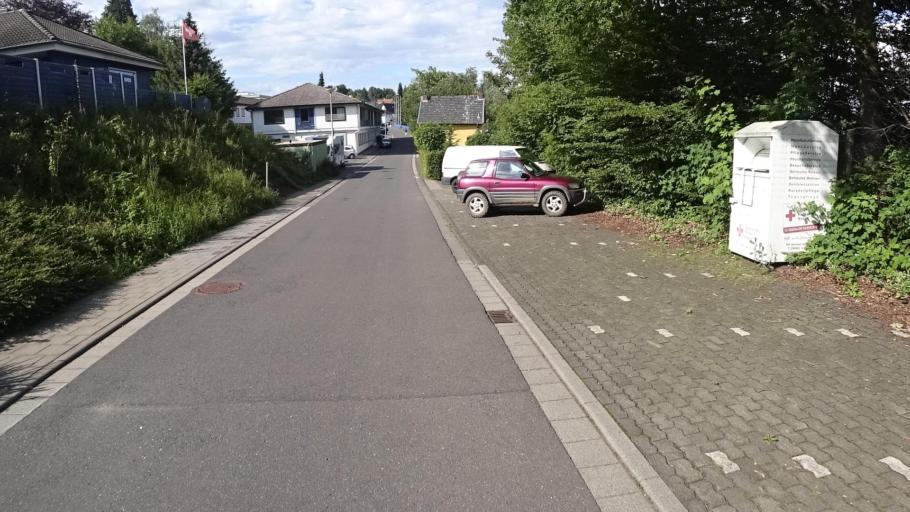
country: DE
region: Rheinland-Pfalz
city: Vettelschoss
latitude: 50.6131
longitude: 7.3414
